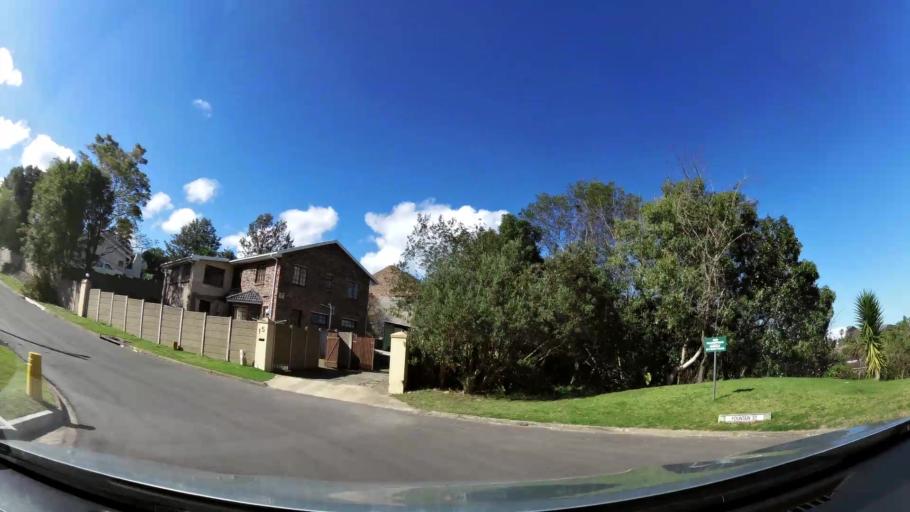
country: ZA
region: Western Cape
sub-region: Eden District Municipality
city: George
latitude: -33.9526
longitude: 22.4757
